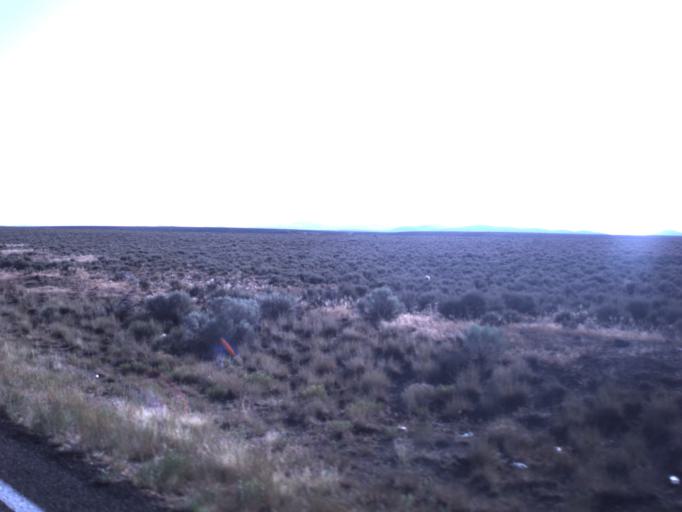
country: US
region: Utah
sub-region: Iron County
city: Enoch
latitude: 37.9646
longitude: -113.0076
